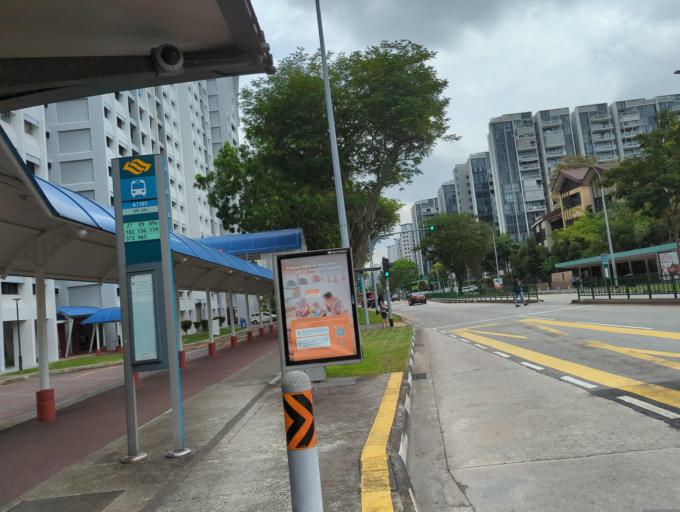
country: MY
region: Johor
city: Kampung Pasir Gudang Baru
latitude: 1.3909
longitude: 103.8977
